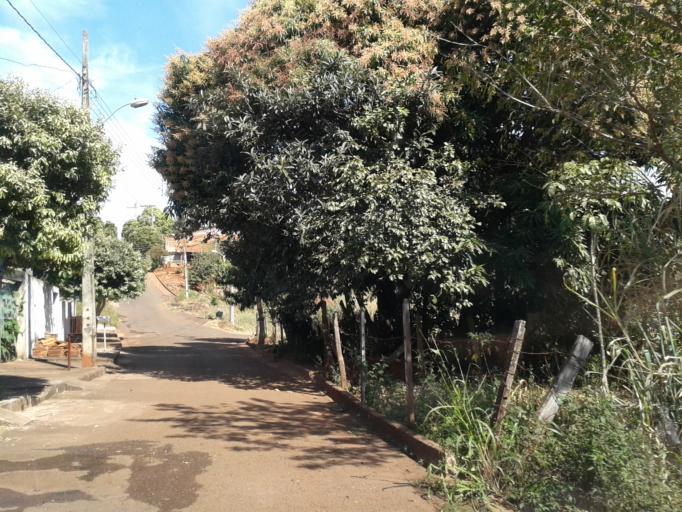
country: BR
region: Minas Gerais
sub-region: Ituiutaba
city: Ituiutaba
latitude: -18.9590
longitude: -49.4674
